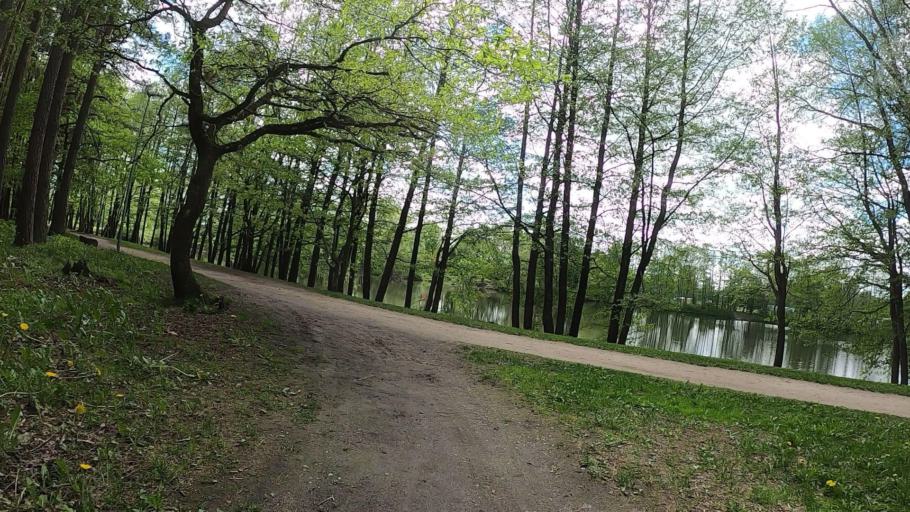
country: LV
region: Babite
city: Pinki
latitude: 56.8784
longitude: 23.9412
